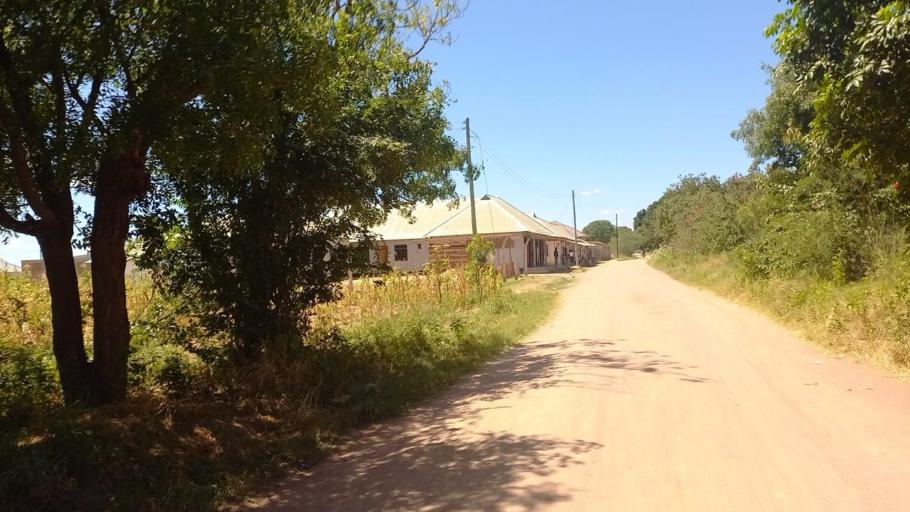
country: TZ
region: Dodoma
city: Dodoma
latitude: -6.1210
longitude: 35.7413
